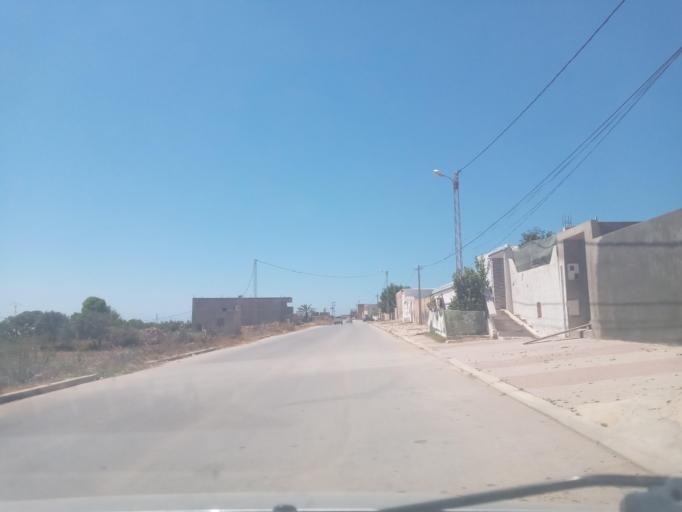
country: TN
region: Nabul
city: El Haouaria
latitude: 37.0516
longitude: 10.9986
